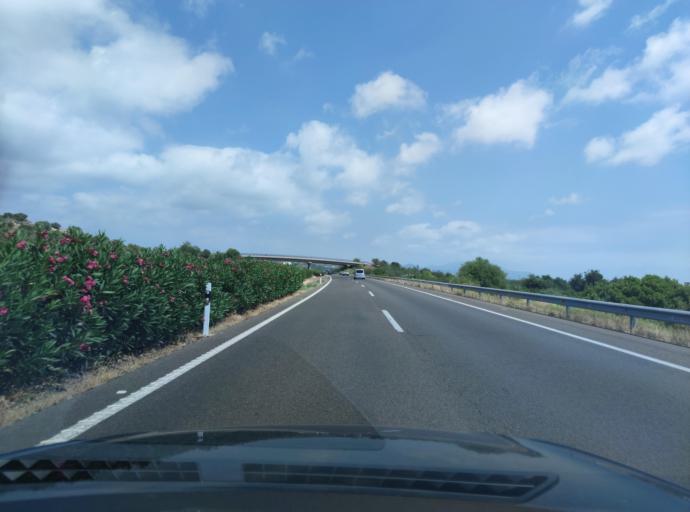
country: ES
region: Valencia
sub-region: Provincia de Castello
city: Benicarlo
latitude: 40.4717
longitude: 0.4181
